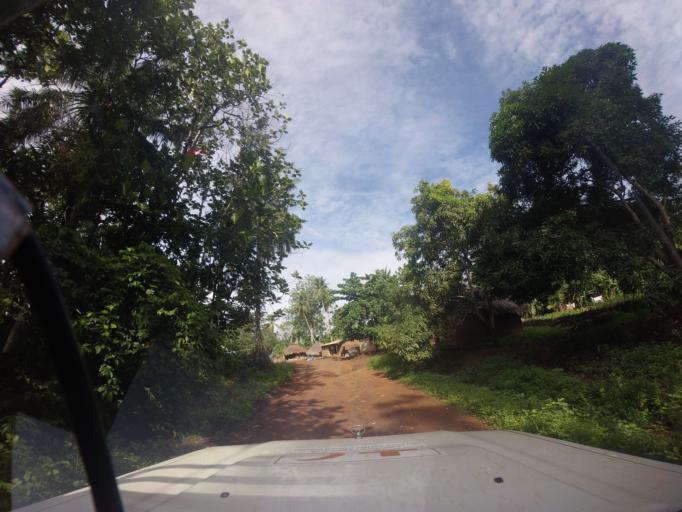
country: SL
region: Northern Province
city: Kambia
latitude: 9.1161
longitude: -12.9473
